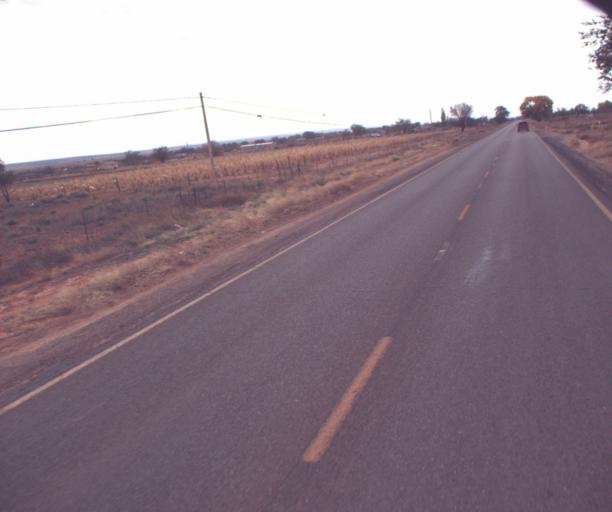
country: US
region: Arizona
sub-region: Apache County
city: Chinle
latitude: 36.2422
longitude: -109.6023
